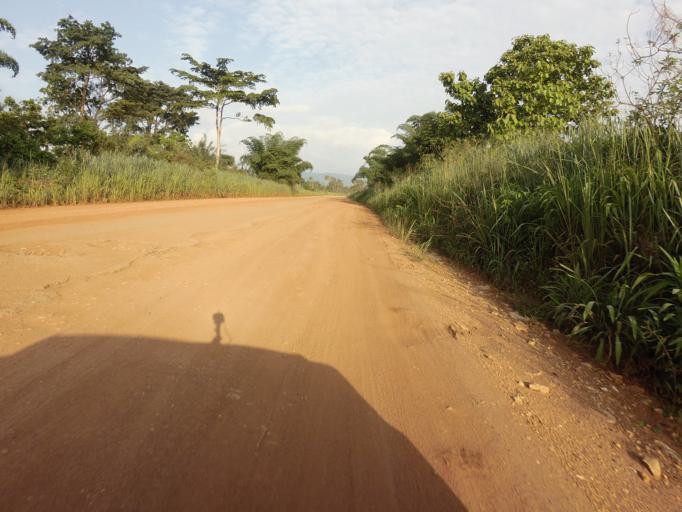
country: GH
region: Volta
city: Kpandu
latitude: 6.9875
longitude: 0.4437
